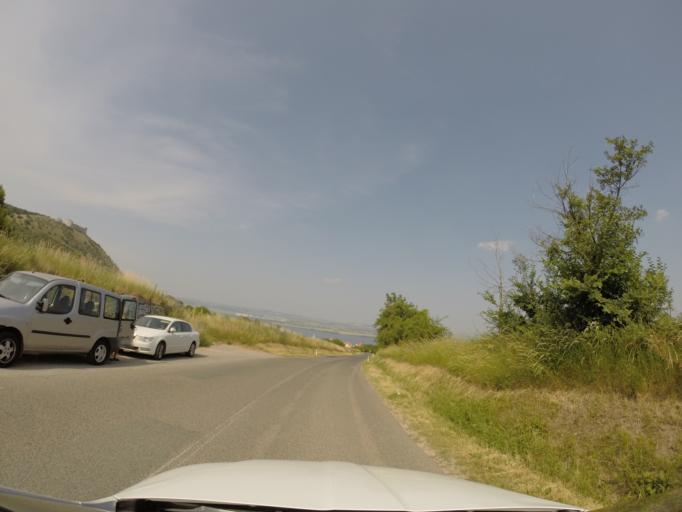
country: CZ
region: South Moravian
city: Sakvice
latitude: 48.8690
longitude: 16.6617
